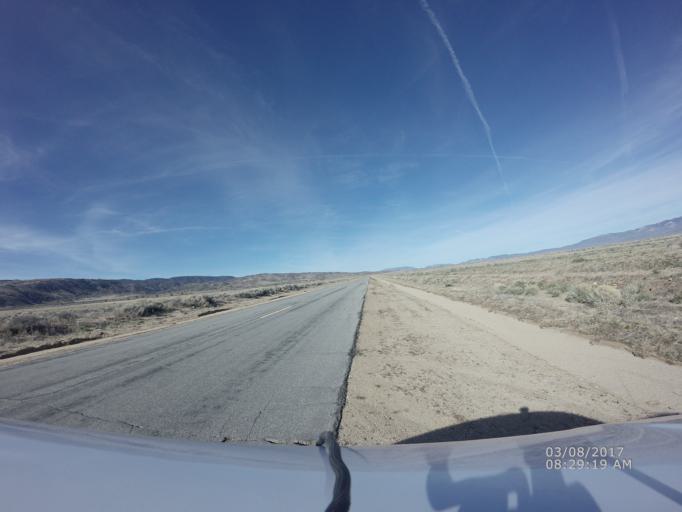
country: US
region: California
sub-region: Los Angeles County
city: Green Valley
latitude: 34.7461
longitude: -118.4734
